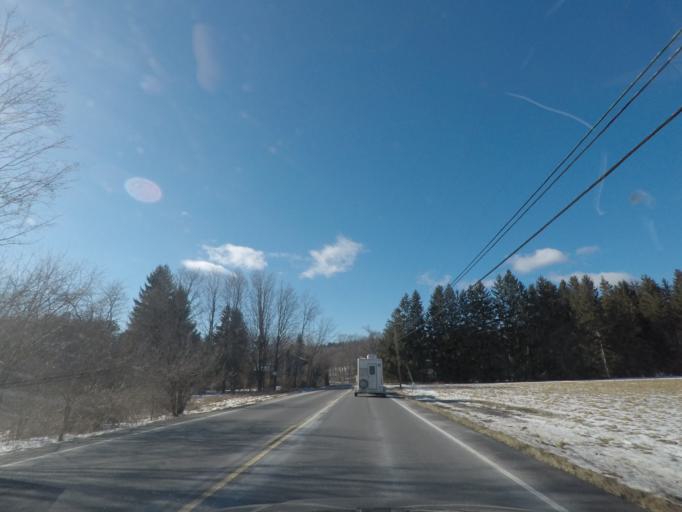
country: US
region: New York
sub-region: Columbia County
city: Chatham
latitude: 42.4203
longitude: -73.4954
